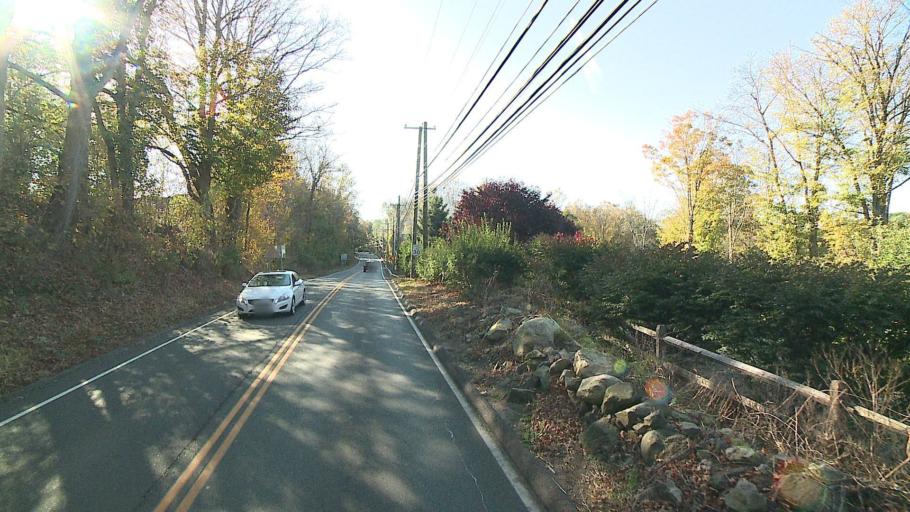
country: US
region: Connecticut
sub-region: Fairfield County
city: Wilton
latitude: 41.2110
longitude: -73.3869
